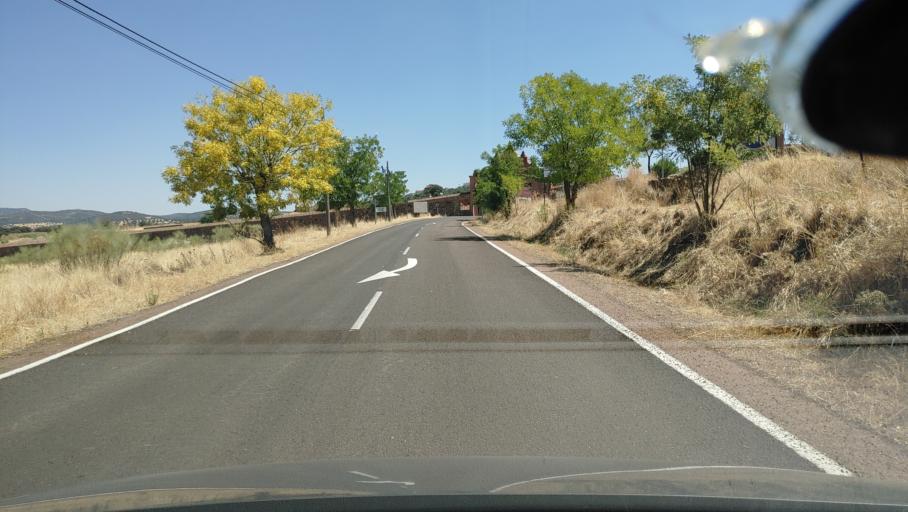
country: ES
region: Castille-La Mancha
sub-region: Provincia de Ciudad Real
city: Alamillo
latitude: 38.7403
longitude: -4.7182
